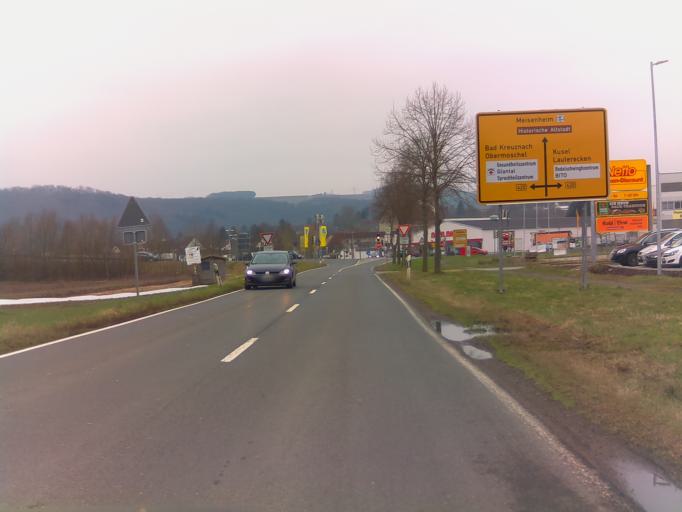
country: DE
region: Rheinland-Pfalz
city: Meisenheim
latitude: 49.7158
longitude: 7.6653
